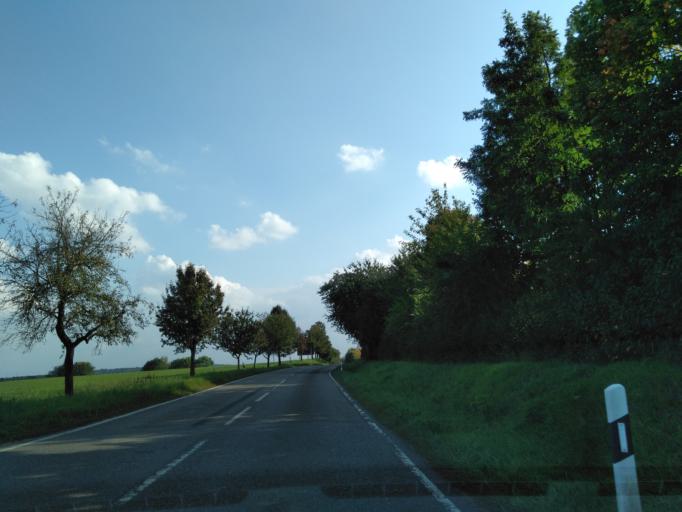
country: DE
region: Baden-Wuerttemberg
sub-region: Regierungsbezirk Stuttgart
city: Sersheim
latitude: 48.9492
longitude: 9.0181
